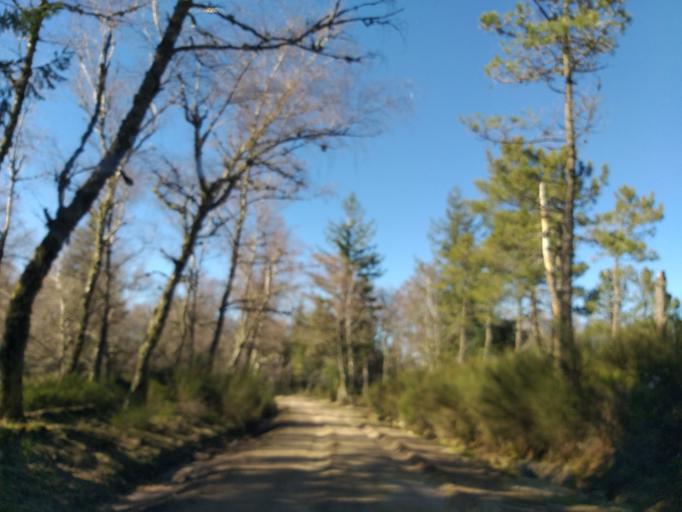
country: PT
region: Guarda
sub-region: Manteigas
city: Manteigas
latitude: 40.4897
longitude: -7.4920
